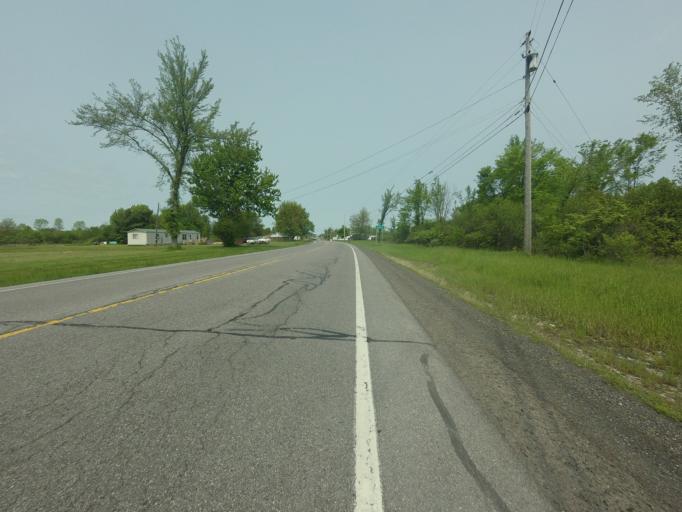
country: US
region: New York
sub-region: Jefferson County
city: Dexter
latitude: 44.0269
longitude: -76.0416
